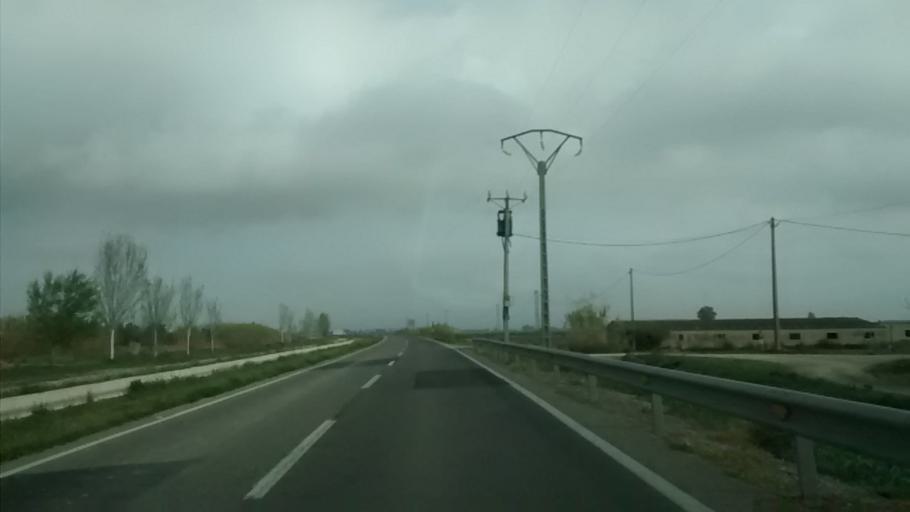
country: ES
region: Catalonia
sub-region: Provincia de Tarragona
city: Sant Carles de la Rapita
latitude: 40.6372
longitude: 0.6016
